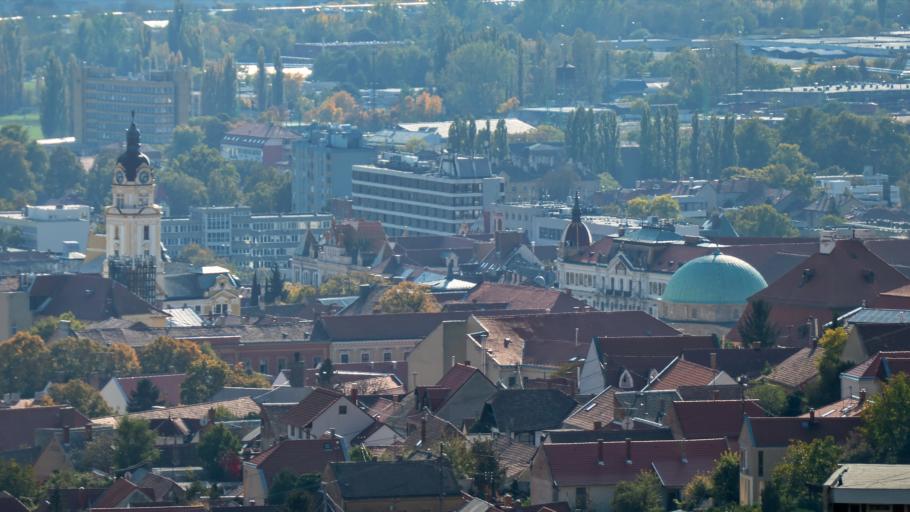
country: HU
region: Baranya
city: Pecs
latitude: 46.0890
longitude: 18.2360
